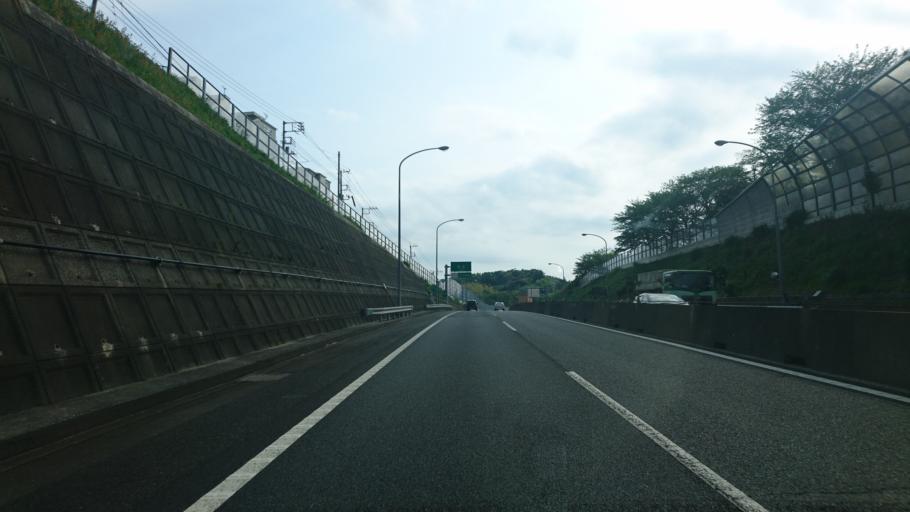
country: JP
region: Kanagawa
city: Yokohama
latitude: 35.4475
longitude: 139.5667
